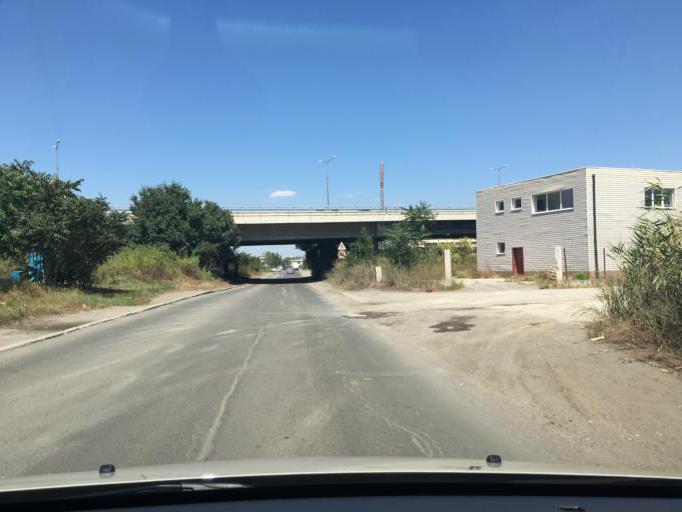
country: BG
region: Burgas
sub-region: Obshtina Burgas
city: Burgas
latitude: 42.4977
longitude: 27.4562
